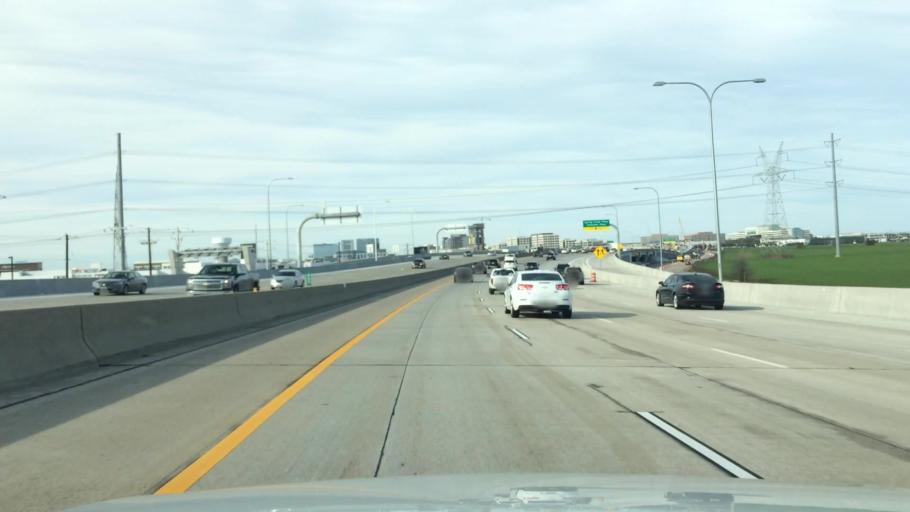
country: US
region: Texas
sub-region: Denton County
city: The Colony
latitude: 33.0567
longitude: -96.8296
